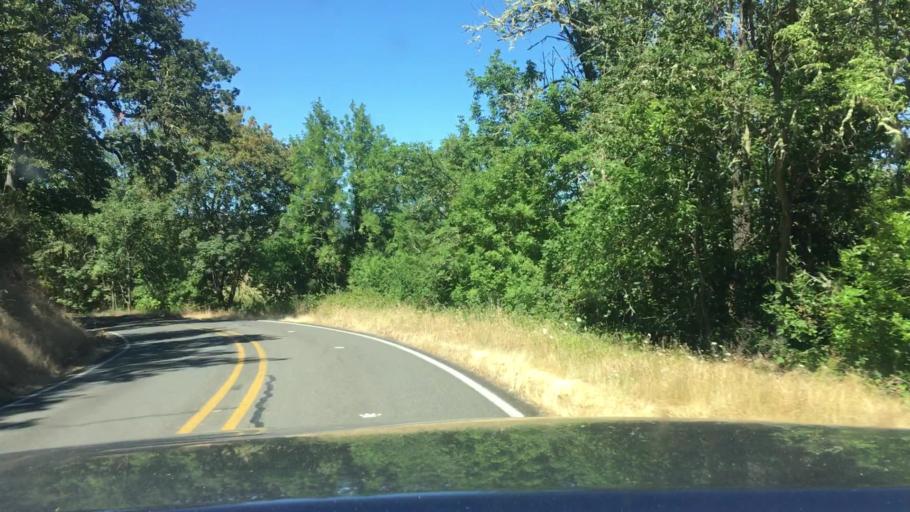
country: US
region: Oregon
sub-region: Douglas County
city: Winston
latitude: 43.1359
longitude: -123.4126
